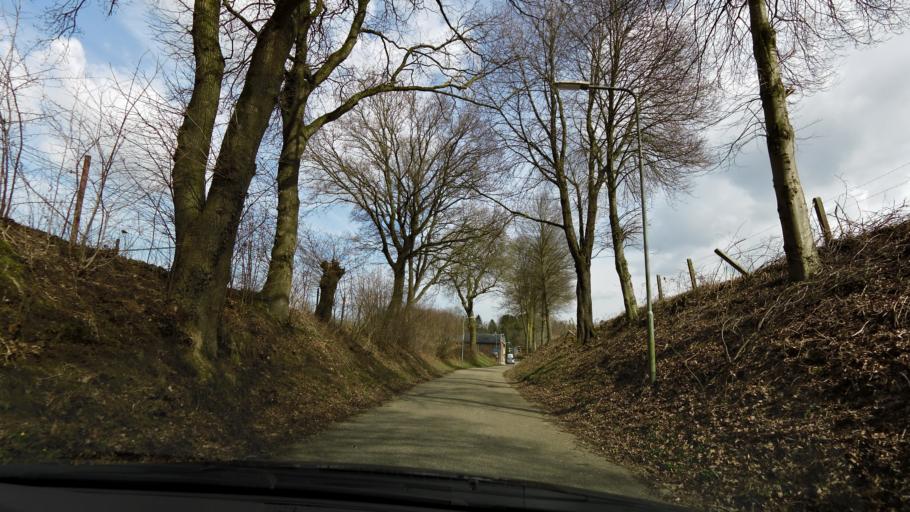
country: NL
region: Limburg
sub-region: Gemeente Simpelveld
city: Simpelveld
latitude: 50.8241
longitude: 5.9980
